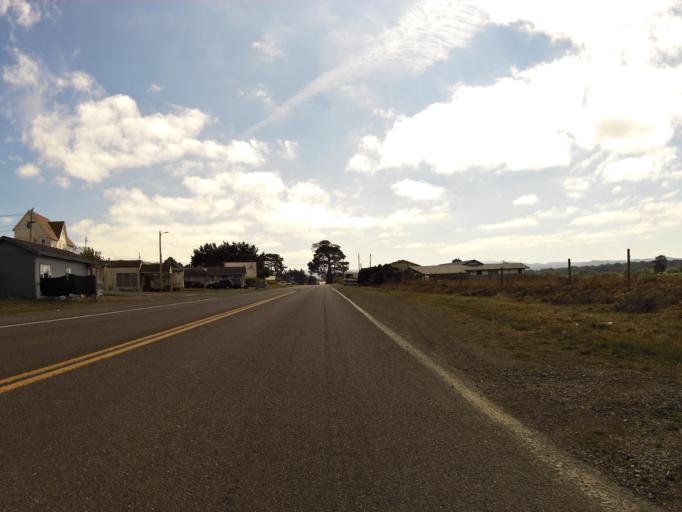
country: US
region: California
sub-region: Humboldt County
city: Ferndale
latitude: 40.6421
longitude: -124.2265
